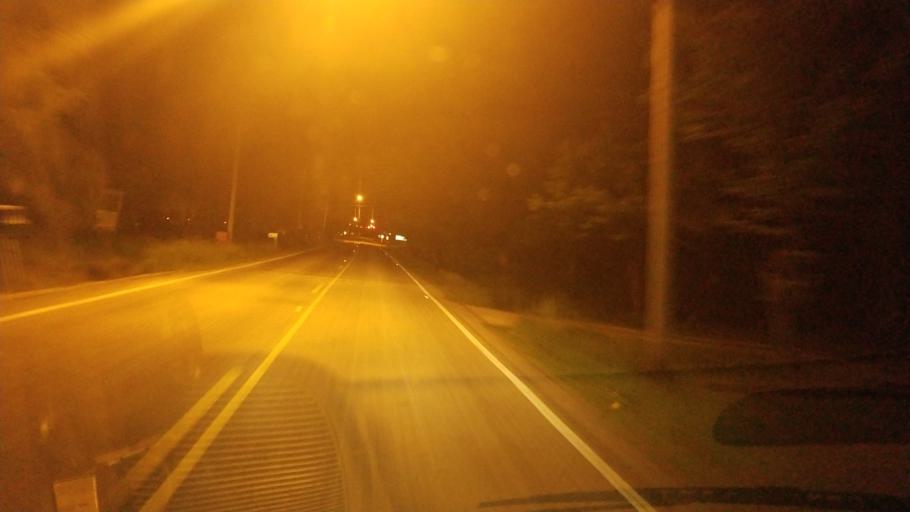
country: US
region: Ohio
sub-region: Ashtabula County
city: Orwell
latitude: 41.5334
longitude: -80.7617
